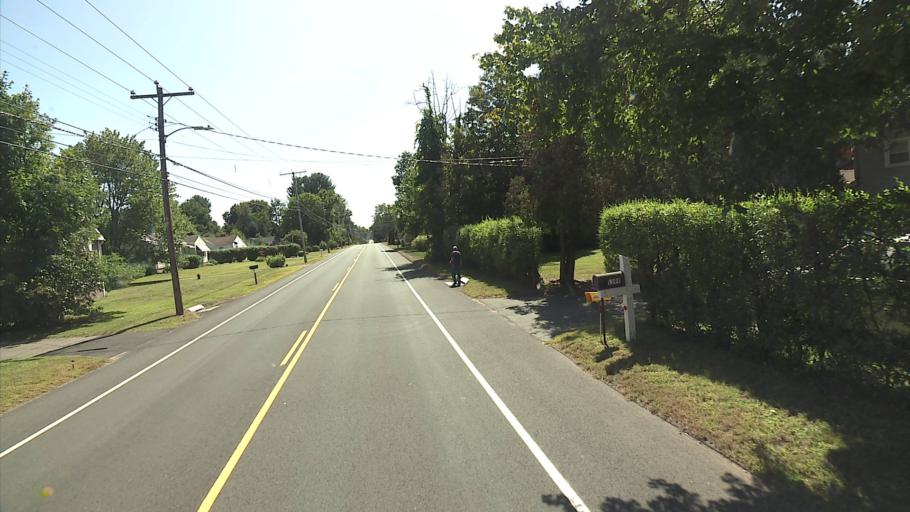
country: US
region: Connecticut
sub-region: Hartford County
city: Windsor Locks
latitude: 41.8995
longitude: -72.6258
